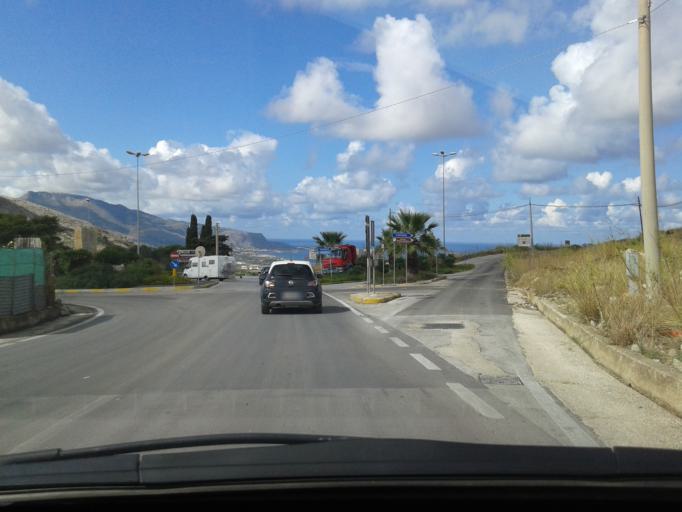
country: IT
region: Sicily
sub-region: Trapani
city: Custonaci
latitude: 38.0764
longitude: 12.6930
